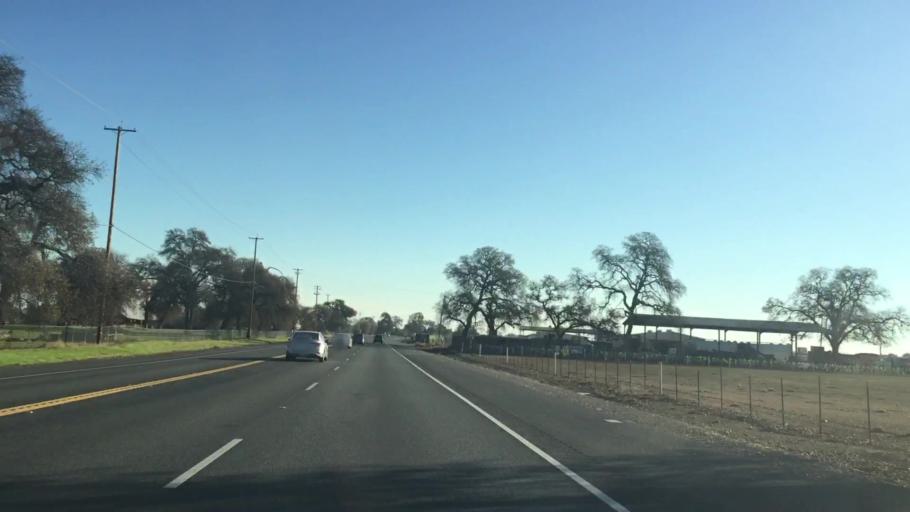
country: US
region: California
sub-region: Butte County
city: Gridley
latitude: 39.3551
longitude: -121.6039
